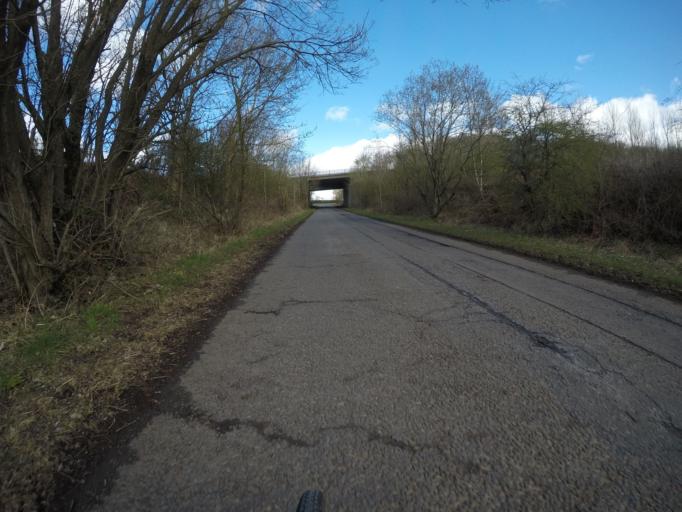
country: GB
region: Scotland
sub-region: East Ayrshire
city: Crosshouse
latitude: 55.6041
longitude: -4.5744
